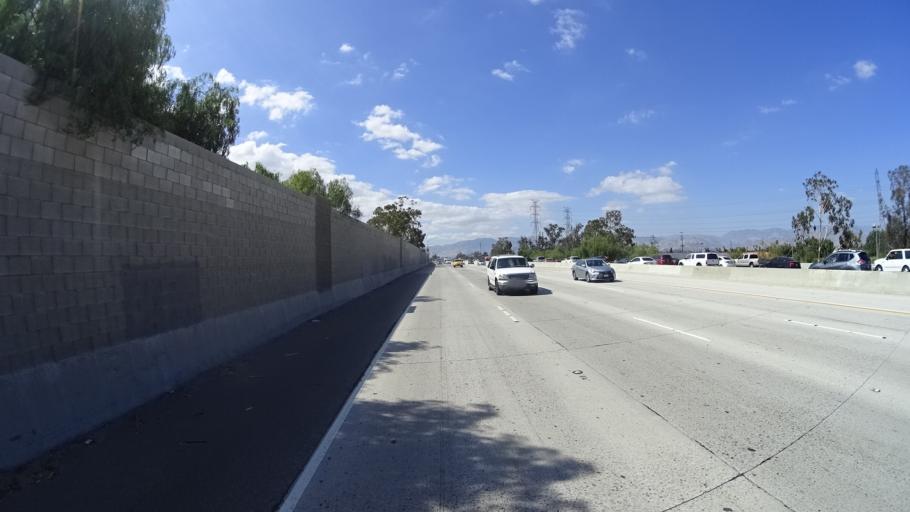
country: US
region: California
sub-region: Los Angeles County
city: Van Nuys
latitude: 34.2152
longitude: -118.4086
